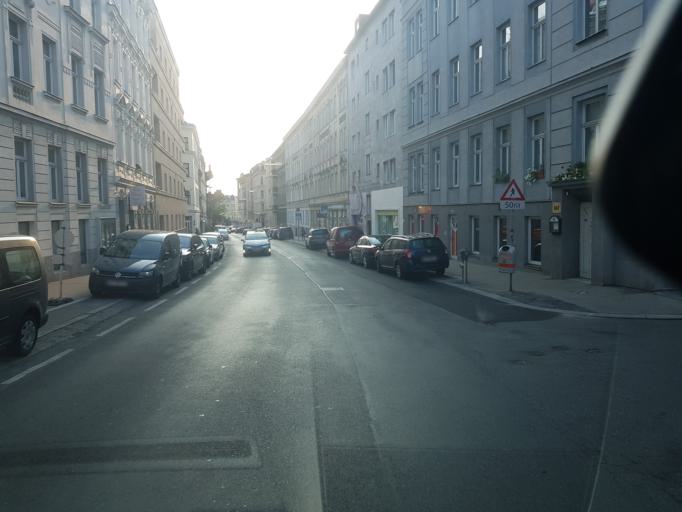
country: AT
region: Vienna
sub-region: Wien Stadt
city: Vienna
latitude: 48.2287
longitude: 16.3321
